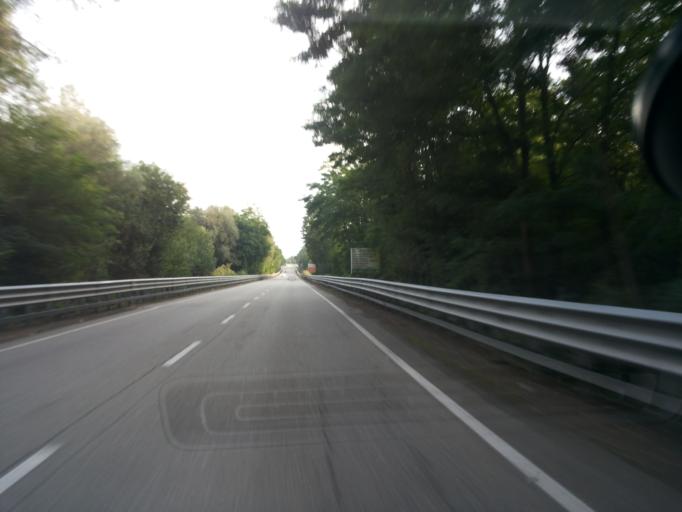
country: IT
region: Piedmont
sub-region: Provincia di Biella
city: Cerreto Castello
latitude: 45.5715
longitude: 8.1694
